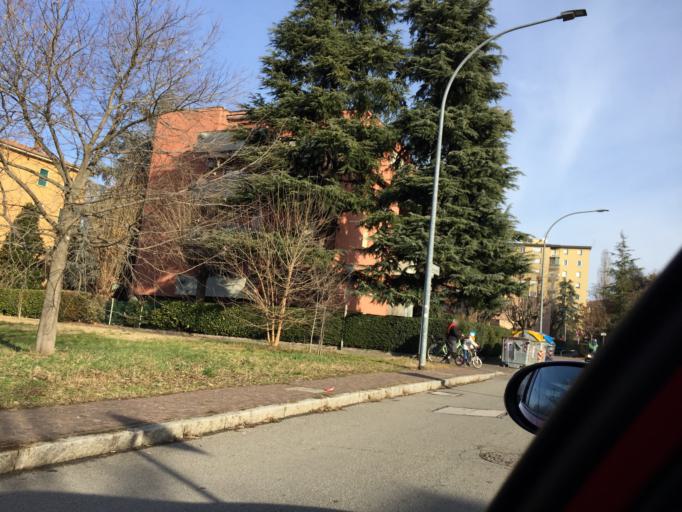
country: IT
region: Emilia-Romagna
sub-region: Provincia di Bologna
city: Casalecchio di Reno
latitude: 44.5008
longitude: 11.2996
